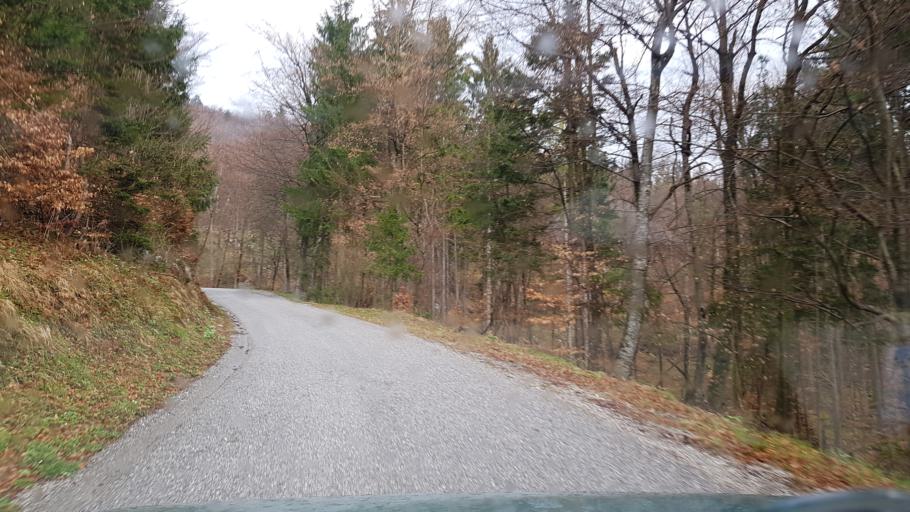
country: SI
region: Cerkno
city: Cerkno
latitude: 46.1291
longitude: 13.8656
